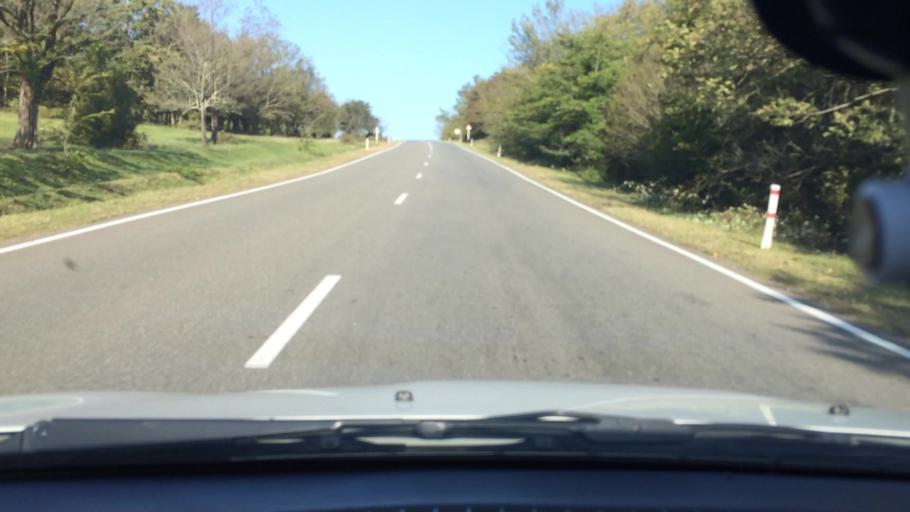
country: GE
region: Imereti
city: Kutaisi
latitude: 42.2506
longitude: 42.7535
